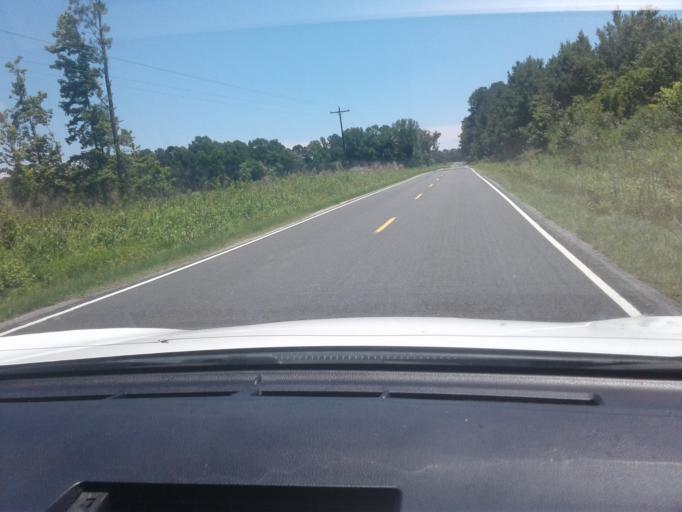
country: US
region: North Carolina
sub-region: Harnett County
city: Buies Creek
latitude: 35.3734
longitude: -78.7596
